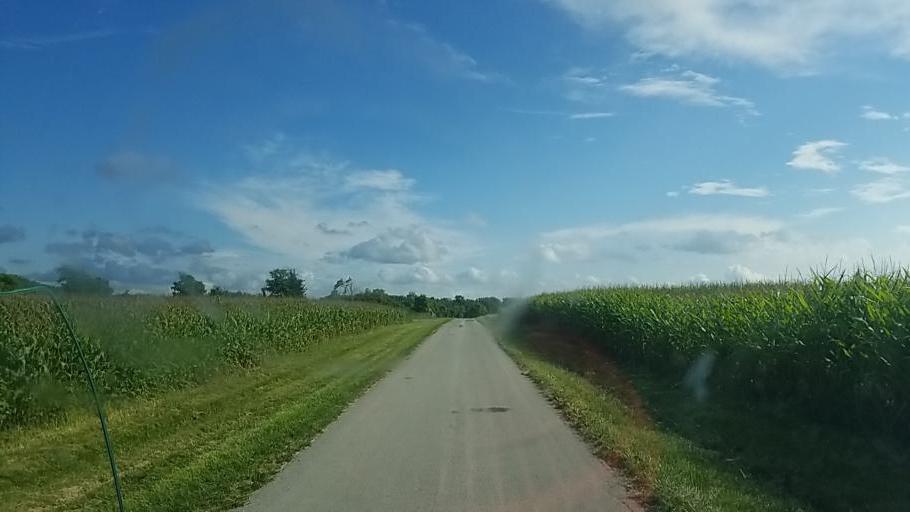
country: US
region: Ohio
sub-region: Wyandot County
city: Upper Sandusky
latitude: 40.7675
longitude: -83.3810
